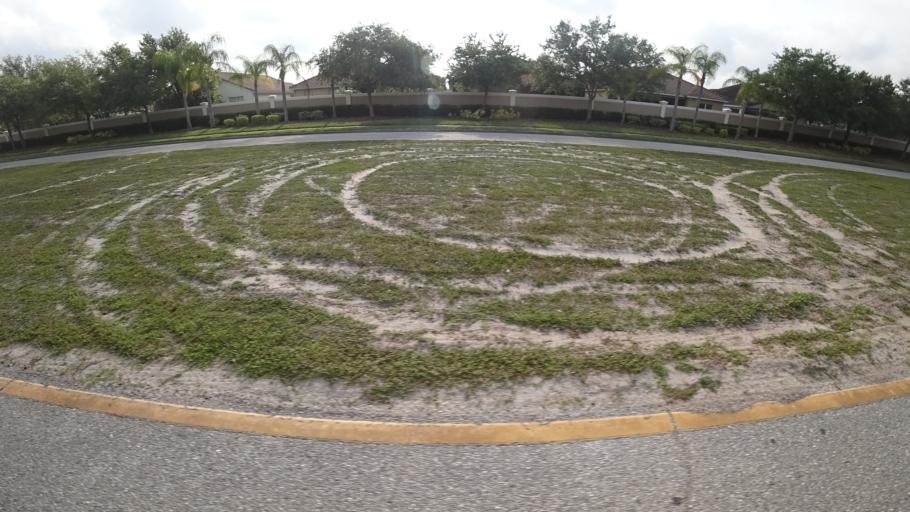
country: US
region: Florida
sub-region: Sarasota County
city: North Sarasota
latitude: 27.4211
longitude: -82.5130
